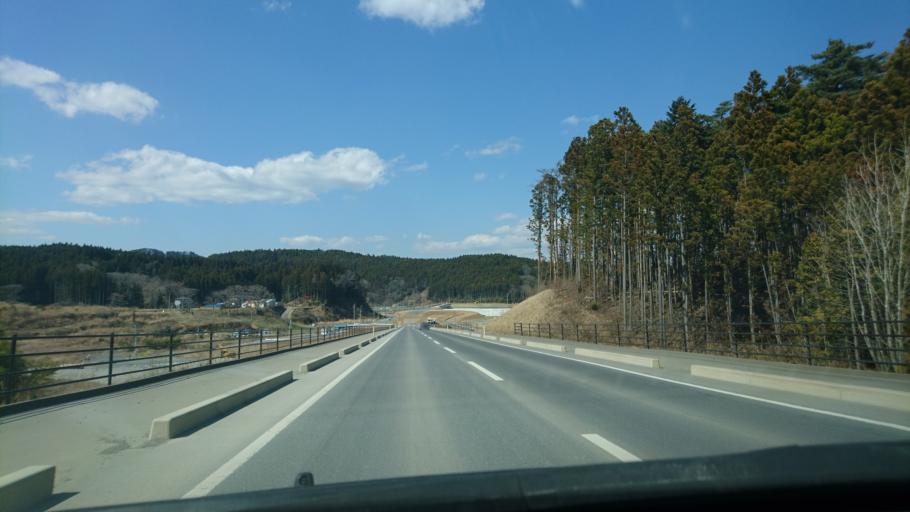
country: JP
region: Miyagi
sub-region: Oshika Gun
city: Onagawa Cho
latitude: 38.6412
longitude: 141.4389
